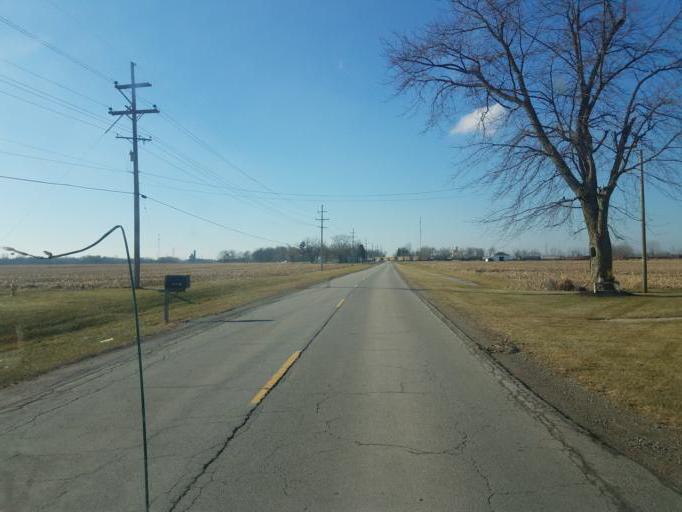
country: US
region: Ohio
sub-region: Marion County
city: Marion
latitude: 40.6294
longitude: -83.1116
